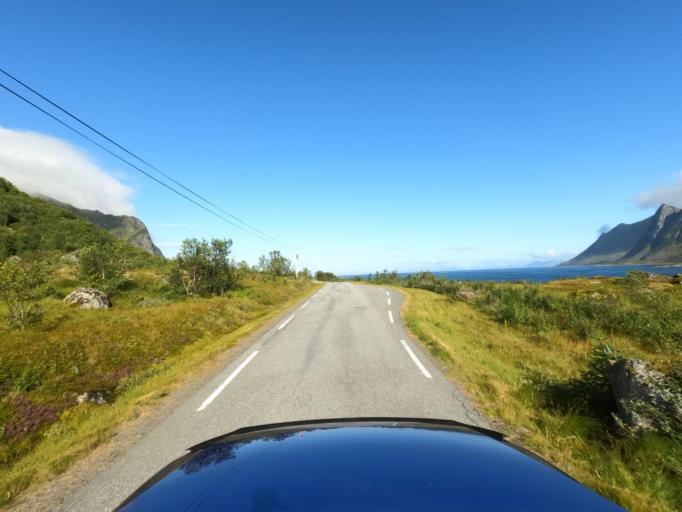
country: NO
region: Nordland
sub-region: Vagan
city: Kabelvag
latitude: 68.2985
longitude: 14.2664
